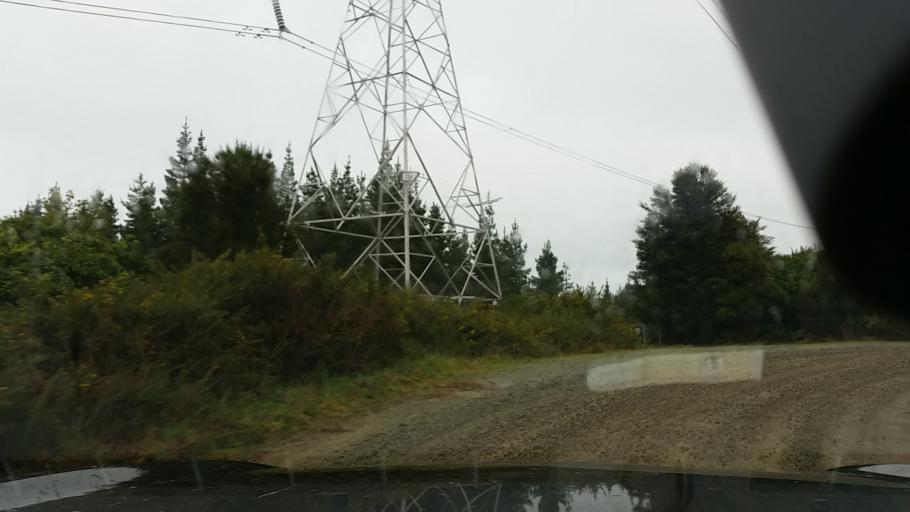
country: NZ
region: Marlborough
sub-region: Marlborough District
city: Picton
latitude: -41.3431
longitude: 174.0851
